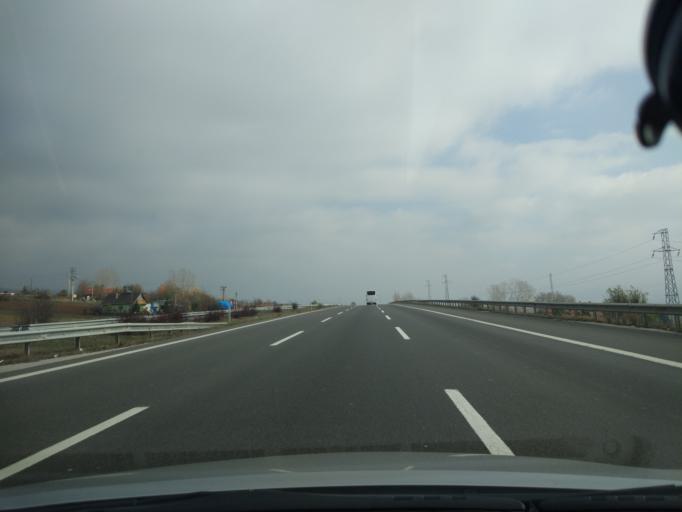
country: TR
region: Bolu
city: Bolu
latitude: 40.7633
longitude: 31.6101
